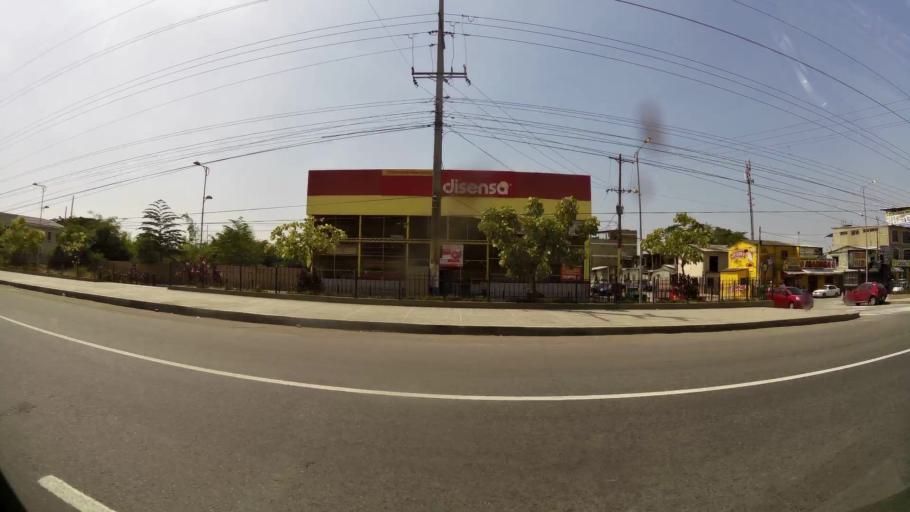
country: EC
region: Guayas
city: Eloy Alfaro
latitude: -2.0521
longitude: -79.8823
